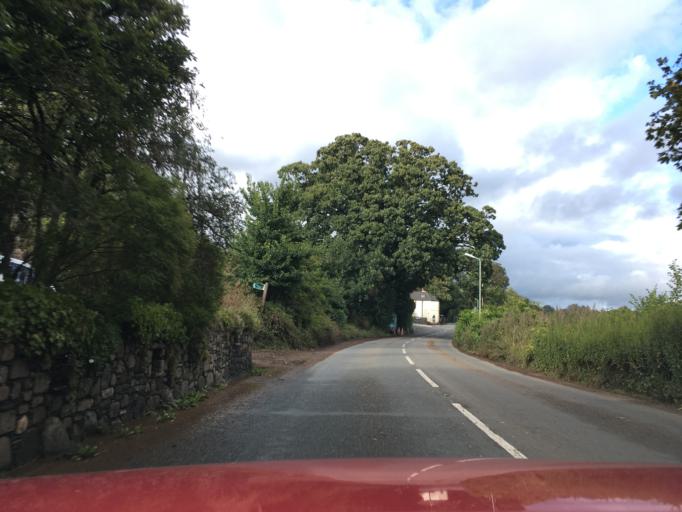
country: GB
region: England
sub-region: Devon
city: Ivybridge
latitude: 50.3589
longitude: -3.9182
